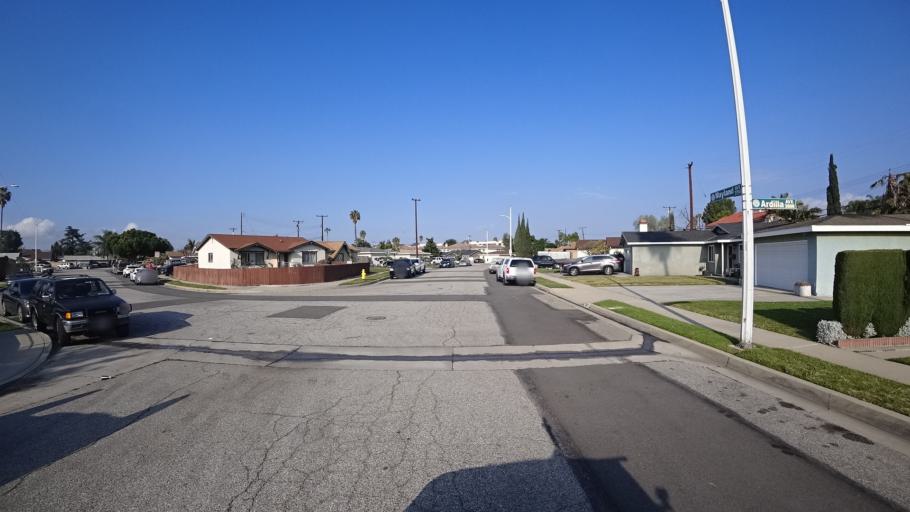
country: US
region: California
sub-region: Los Angeles County
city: Baldwin Park
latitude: 34.0792
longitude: -117.9488
